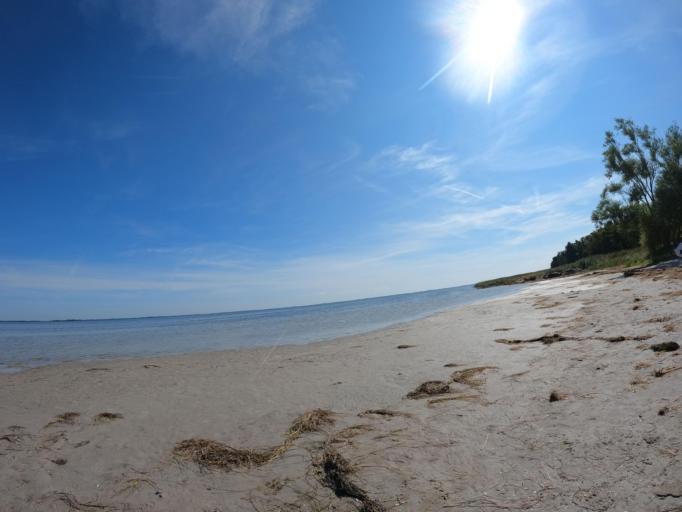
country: DE
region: Mecklenburg-Vorpommern
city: Prohn
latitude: 54.4333
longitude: 13.0333
